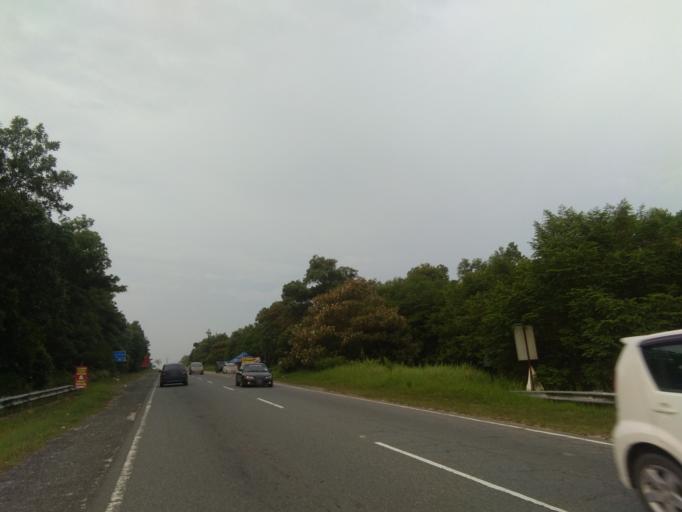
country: MY
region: Penang
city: Tasek Glugor
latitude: 5.5096
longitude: 100.6263
